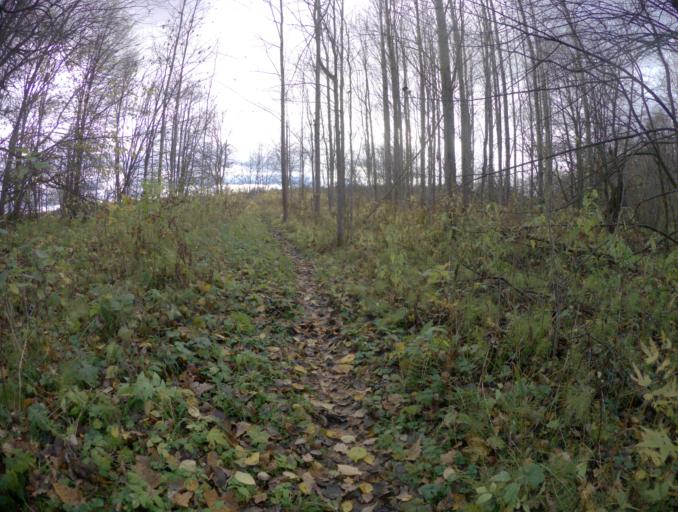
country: RU
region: Vladimir
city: Raduzhnyy
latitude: 56.0528
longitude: 40.3264
